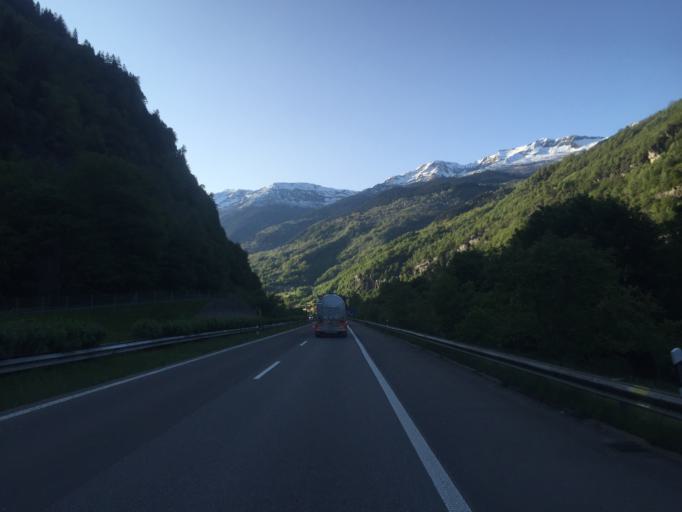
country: CH
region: Ticino
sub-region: Leventina District
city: Faido
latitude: 46.4560
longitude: 8.8265
